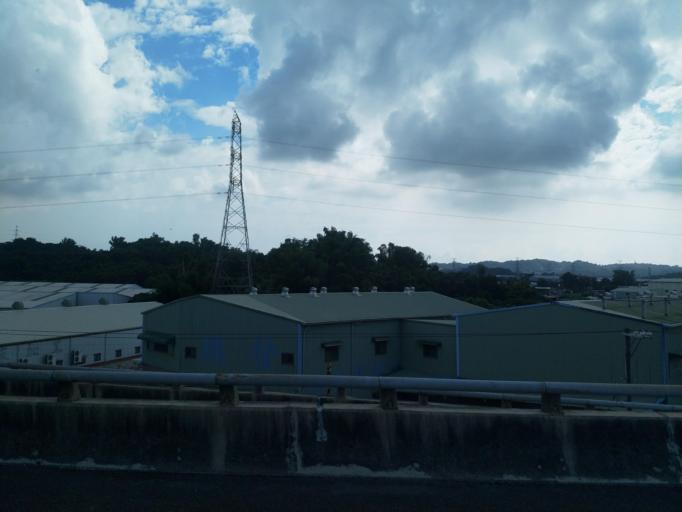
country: TW
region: Taiwan
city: Fengshan
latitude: 22.7079
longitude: 120.3605
